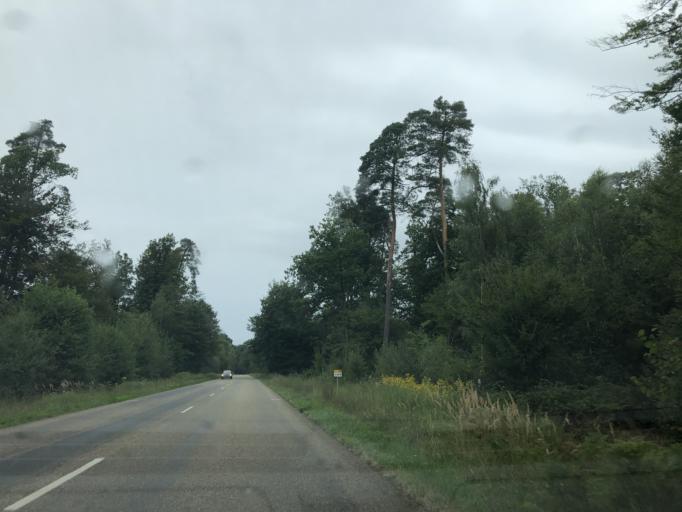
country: DE
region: Rheinland-Pfalz
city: Scheibenhardt
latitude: 48.9908
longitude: 8.0816
